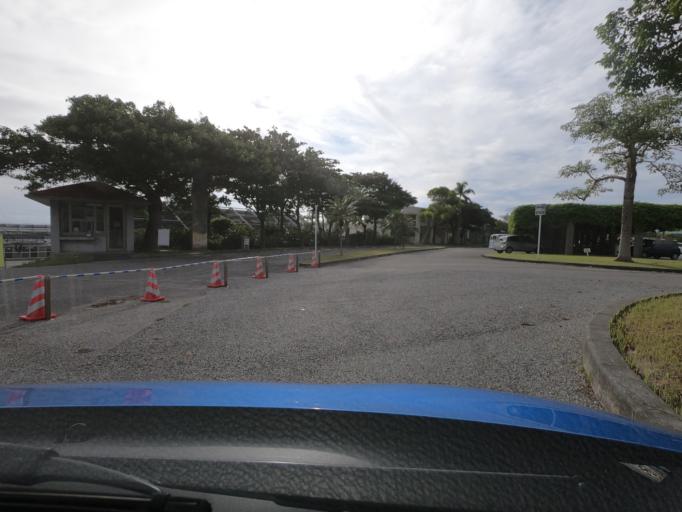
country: JP
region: Okinawa
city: Nago
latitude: 26.6808
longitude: 127.8841
